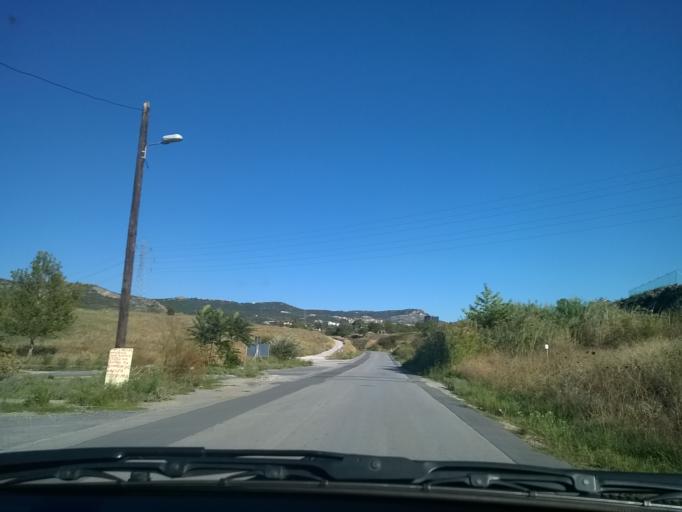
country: GR
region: Central Macedonia
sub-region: Nomos Thessalonikis
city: Polichni
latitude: 40.6661
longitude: 22.9602
